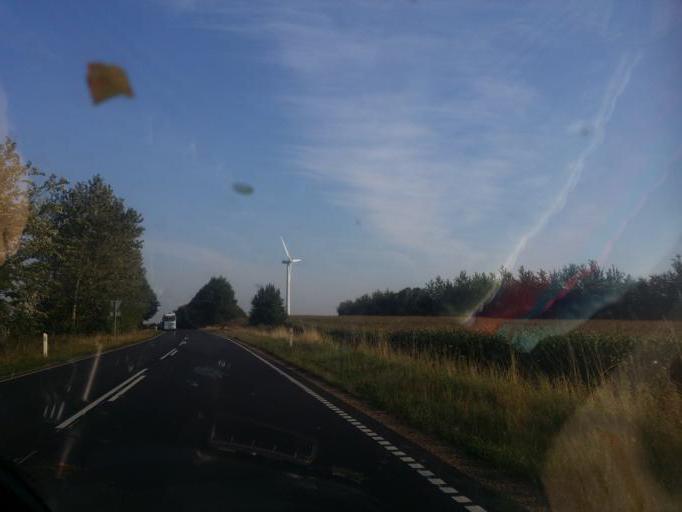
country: DK
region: South Denmark
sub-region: Tonder Kommune
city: Tonder
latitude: 54.9529
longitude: 8.8875
